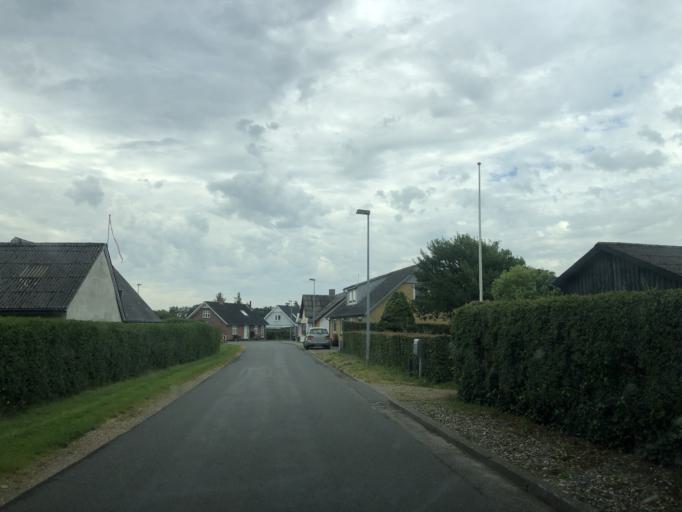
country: DK
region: Central Jutland
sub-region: Holstebro Kommune
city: Holstebro
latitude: 56.3776
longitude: 8.5225
